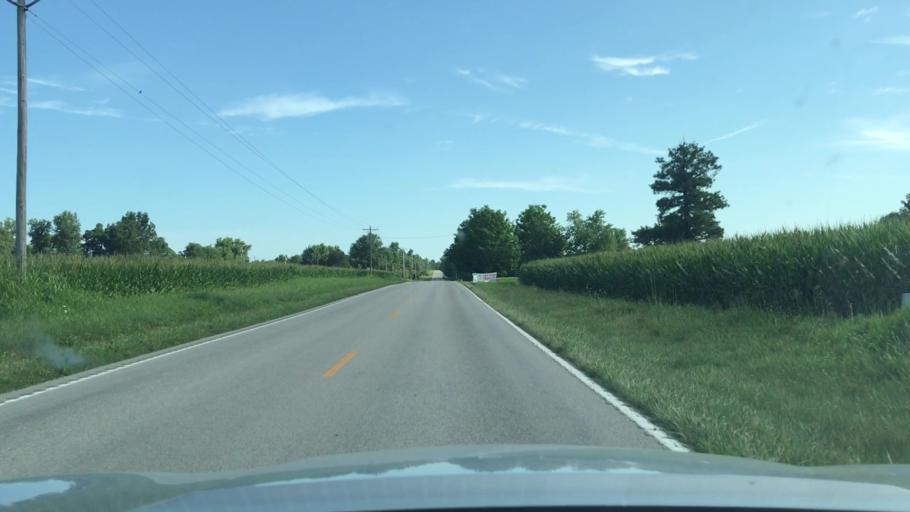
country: US
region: Kentucky
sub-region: Todd County
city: Elkton
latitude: 36.9217
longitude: -87.1627
